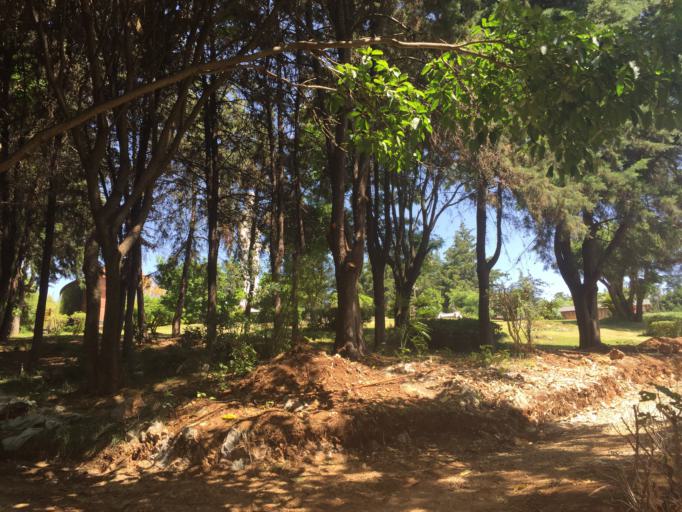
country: CN
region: Yunnan
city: Yuhu
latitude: 25.9047
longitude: 100.1909
